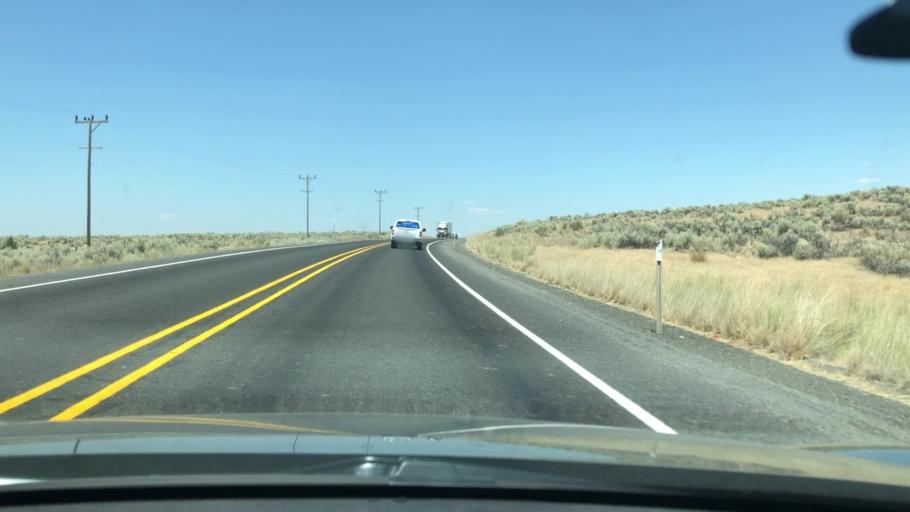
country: US
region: Idaho
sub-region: Owyhee County
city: Murphy
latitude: 42.9954
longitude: -117.0610
